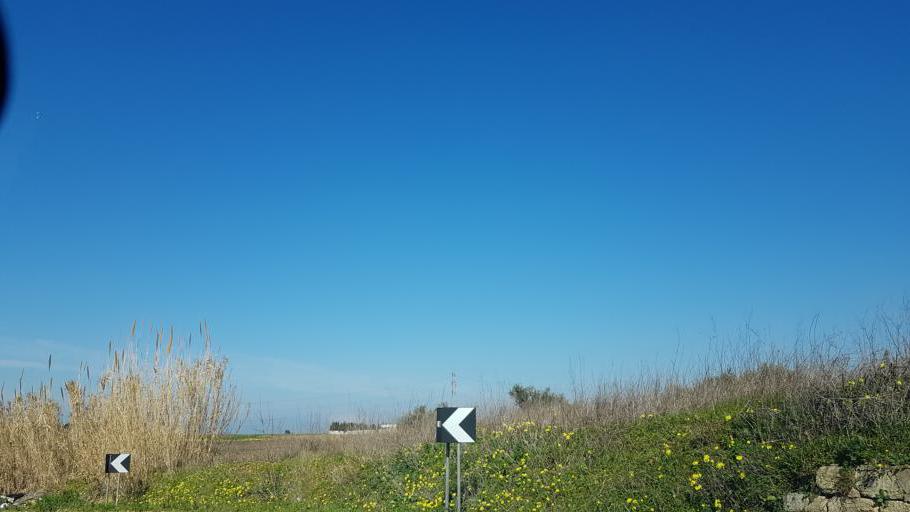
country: IT
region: Apulia
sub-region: Provincia di Brindisi
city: La Rosa
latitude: 40.5917
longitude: 17.9197
